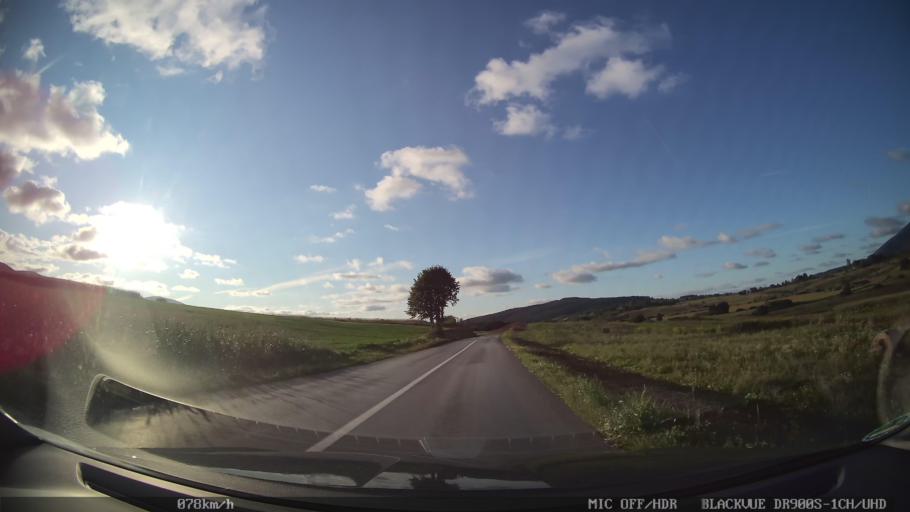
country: HR
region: Karlovacka
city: Plaski
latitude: 45.0910
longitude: 15.3604
